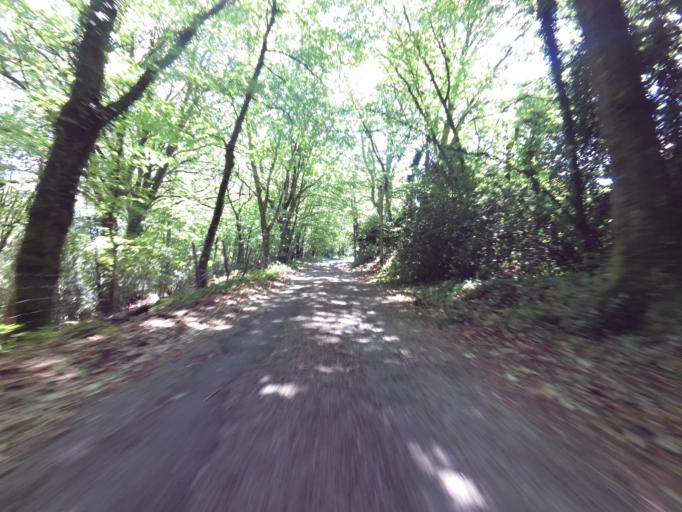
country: FR
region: Brittany
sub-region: Departement du Morbihan
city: Pluherlin
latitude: 47.7018
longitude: -2.3482
